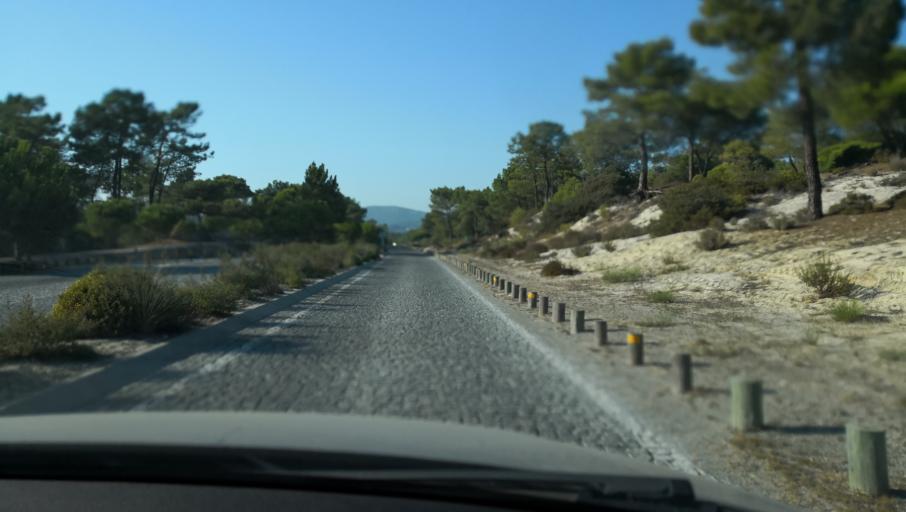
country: PT
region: Setubal
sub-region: Setubal
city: Setubal
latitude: 38.4814
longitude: -8.8912
